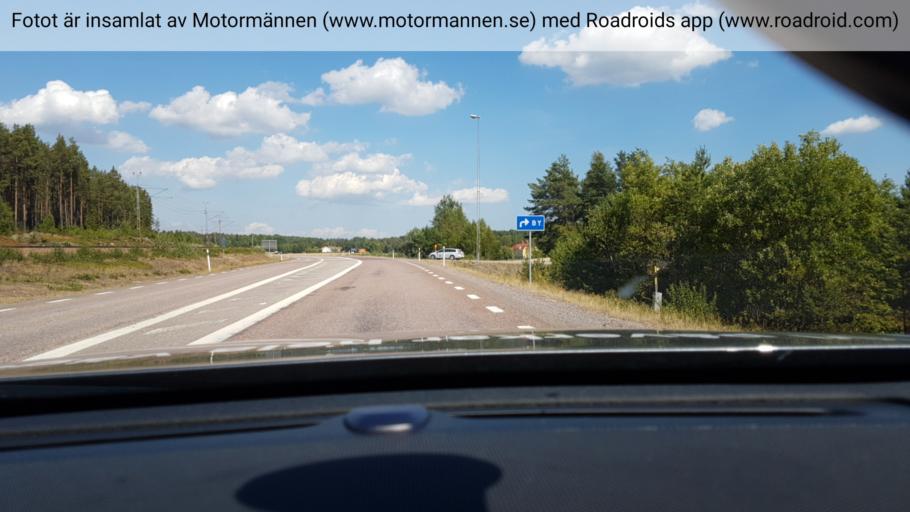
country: SE
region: Dalarna
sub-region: Avesta Kommun
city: Horndal
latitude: 60.2711
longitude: 16.4043
